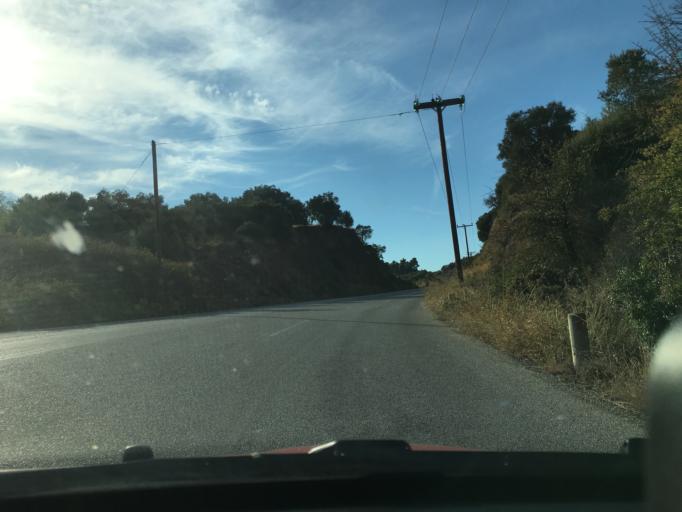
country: GR
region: Central Macedonia
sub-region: Nomos Chalkidikis
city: Agios Nikolaos
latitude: 40.2877
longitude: 23.6878
